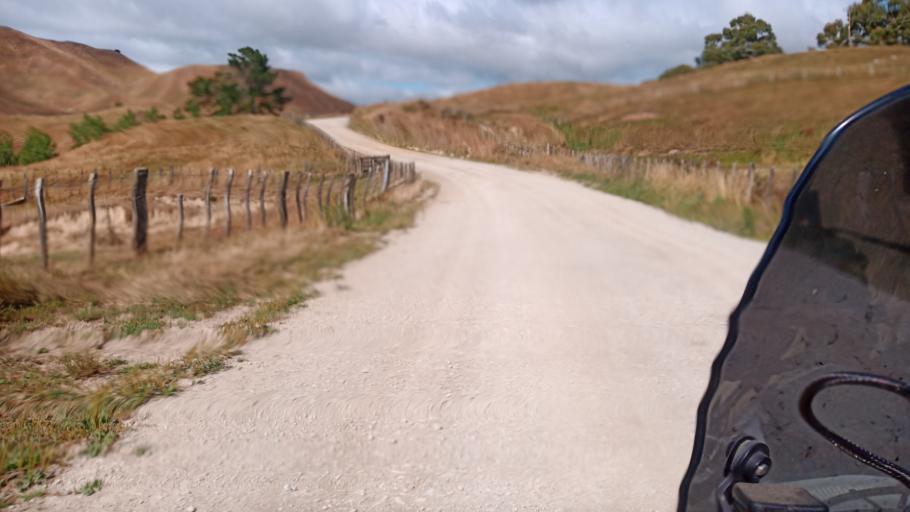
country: NZ
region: Hawke's Bay
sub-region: Wairoa District
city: Wairoa
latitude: -38.6065
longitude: 177.4522
